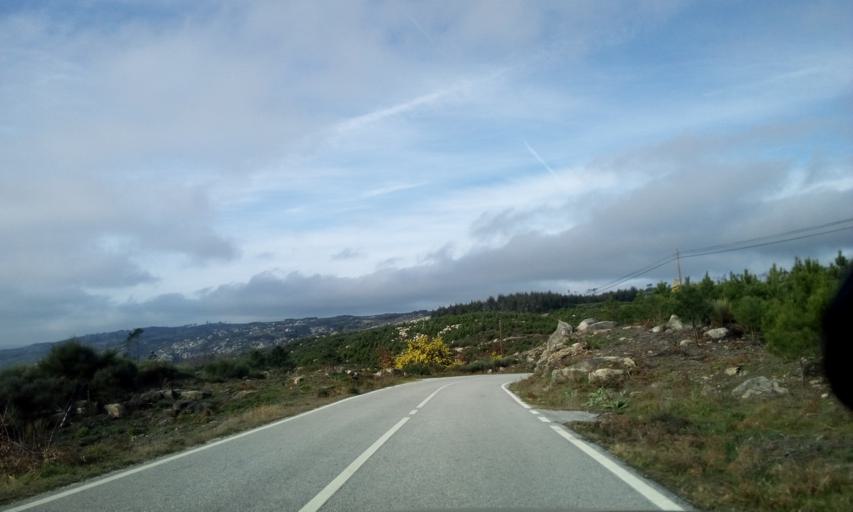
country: PT
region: Guarda
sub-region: Aguiar da Beira
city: Aguiar da Beira
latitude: 40.7511
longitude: -7.5468
